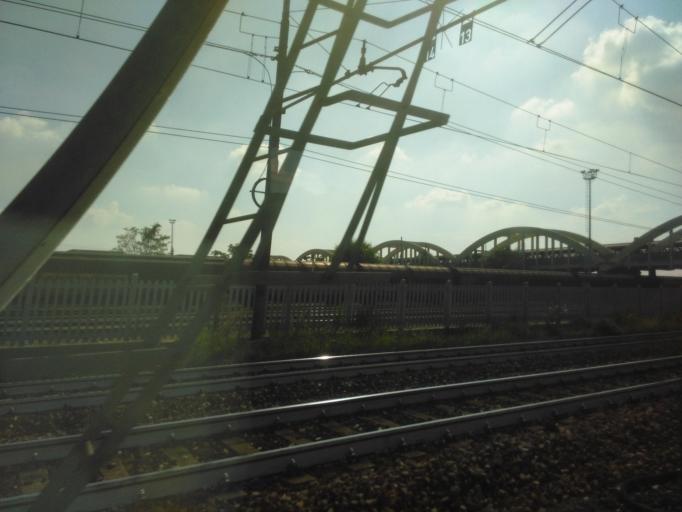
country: IT
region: Lombardy
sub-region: Citta metropolitana di Milano
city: Segrate
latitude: 45.4810
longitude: 9.3015
